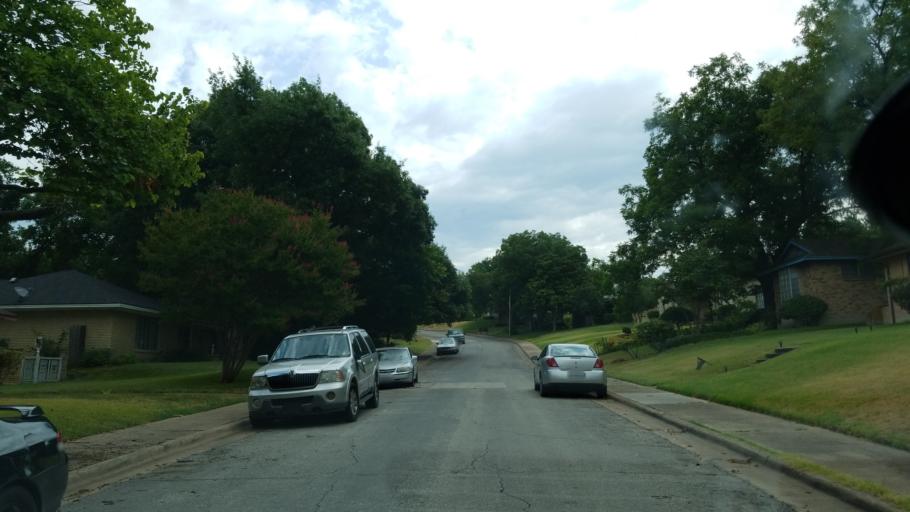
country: US
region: Texas
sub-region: Dallas County
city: Duncanville
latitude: 32.6653
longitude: -96.8426
